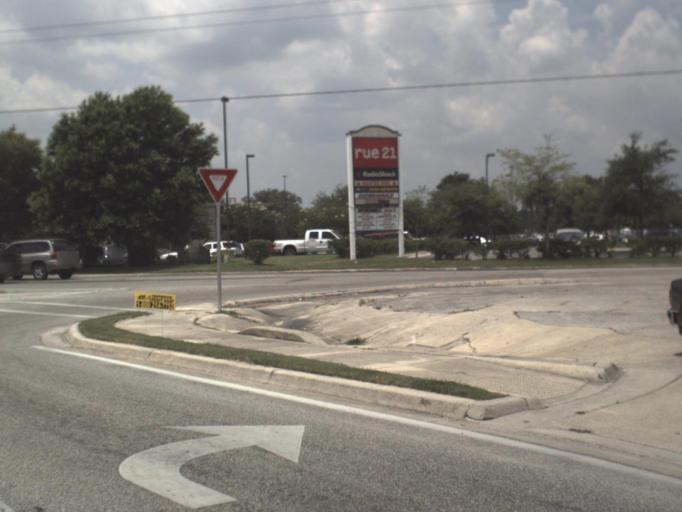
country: US
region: Florida
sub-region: Putnam County
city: Palatka
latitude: 29.6374
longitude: -81.6784
